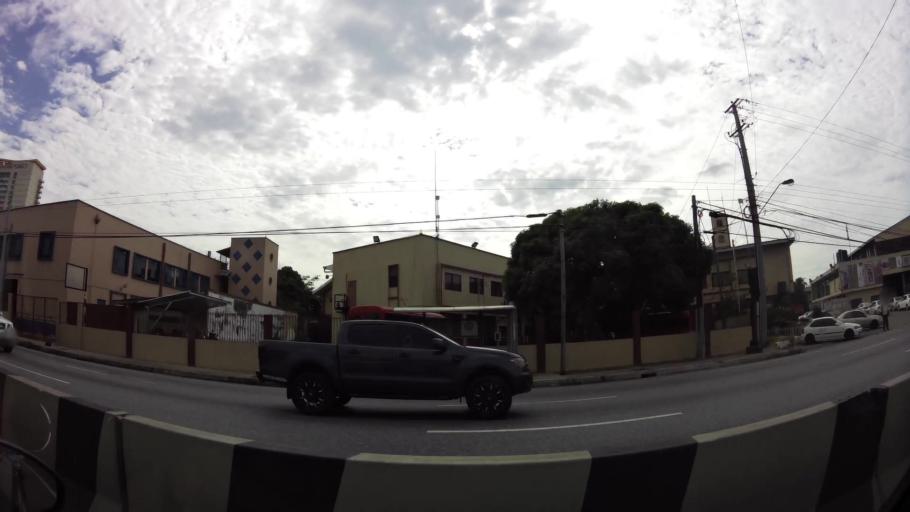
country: TT
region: City of Port of Spain
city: Port-of-Spain
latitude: 10.6528
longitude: -61.5166
